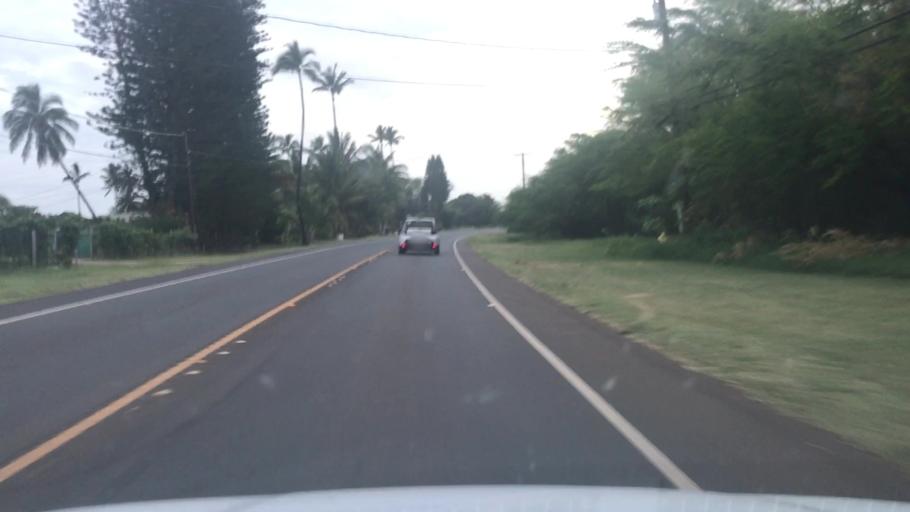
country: US
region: Hawaii
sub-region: Maui County
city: Kaunakakai
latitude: 21.0672
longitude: -156.9565
